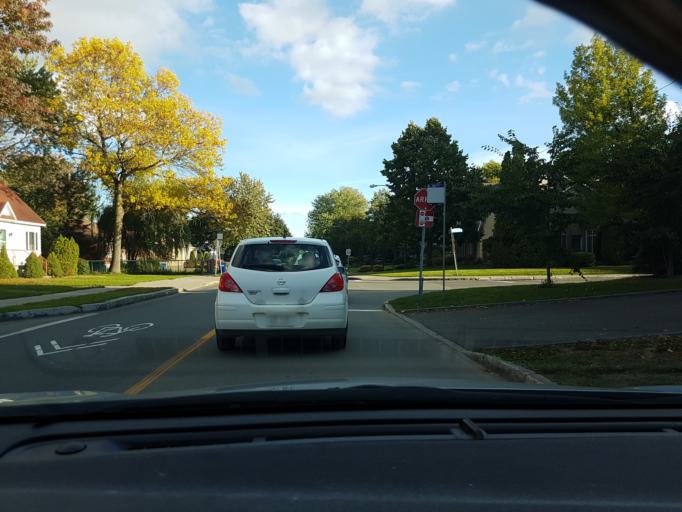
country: CA
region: Quebec
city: Quebec
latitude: 46.7733
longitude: -71.2716
